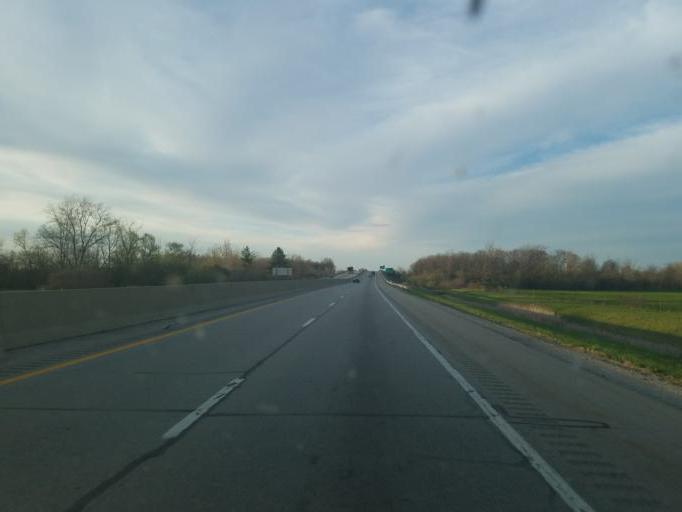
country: US
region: Ohio
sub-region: Wood County
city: Millbury
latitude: 41.5482
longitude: -83.4616
